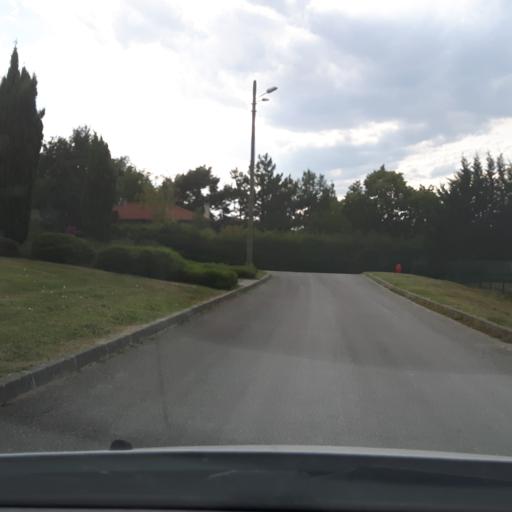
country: FR
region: Midi-Pyrenees
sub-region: Departement de la Haute-Garonne
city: Fronton
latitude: 43.8357
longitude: 1.3869
